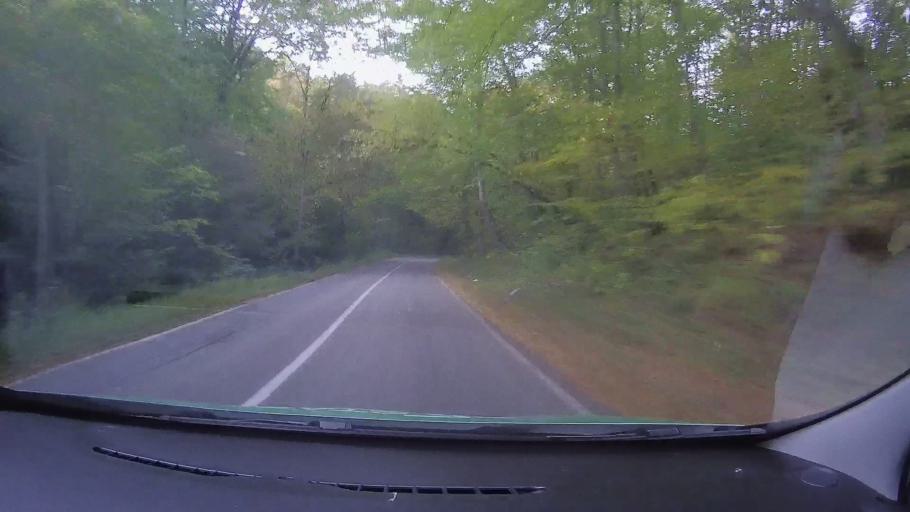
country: RO
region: Timis
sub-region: Comuna Fardea
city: Fardea
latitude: 45.6902
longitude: 22.1566
